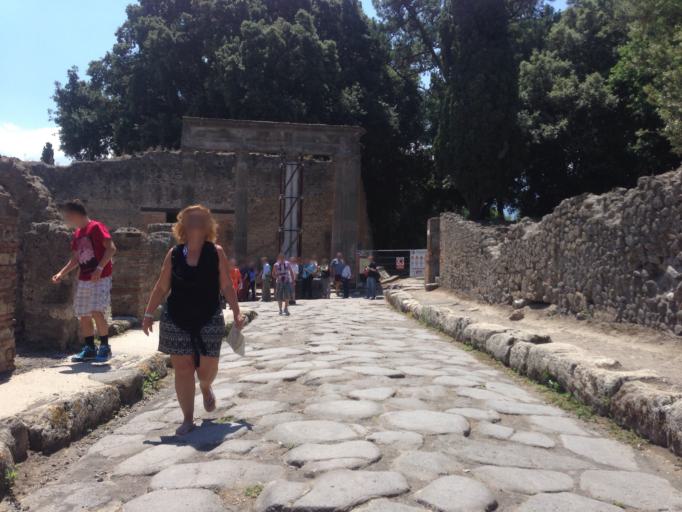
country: IT
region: Campania
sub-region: Provincia di Napoli
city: Pompei
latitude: 40.7492
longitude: 14.4875
